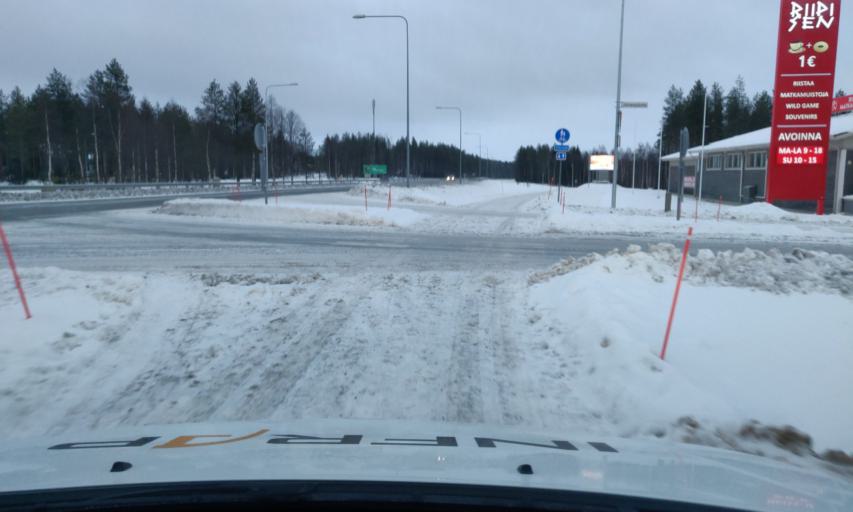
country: FI
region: Northern Ostrobothnia
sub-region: Koillismaa
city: Kuusamo
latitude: 65.9900
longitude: 29.1562
